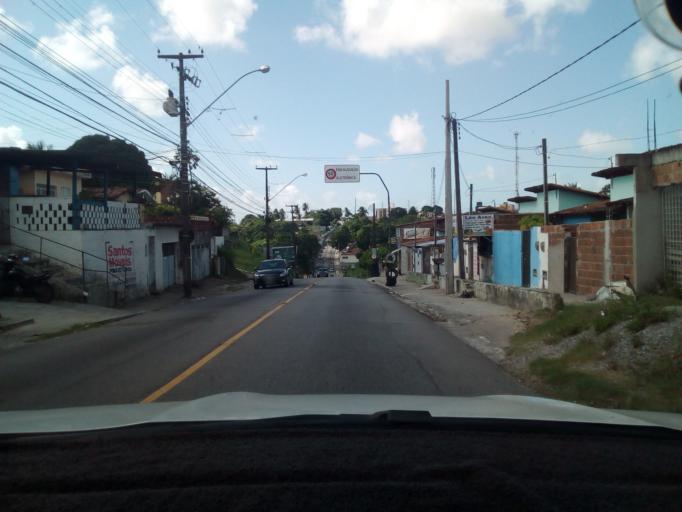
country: BR
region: Paraiba
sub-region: Joao Pessoa
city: Joao Pessoa
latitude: -7.1122
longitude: -34.8713
